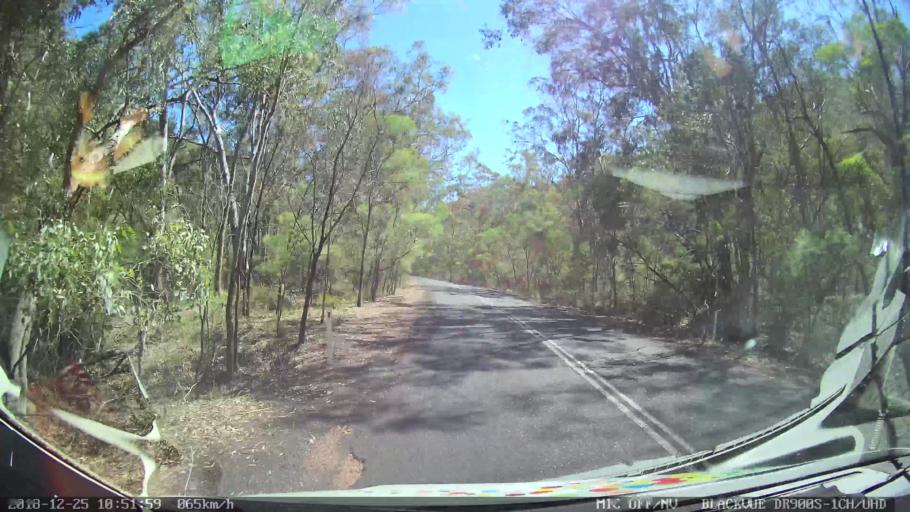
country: AU
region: New South Wales
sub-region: Upper Hunter Shire
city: Merriwa
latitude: -32.4327
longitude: 150.2725
